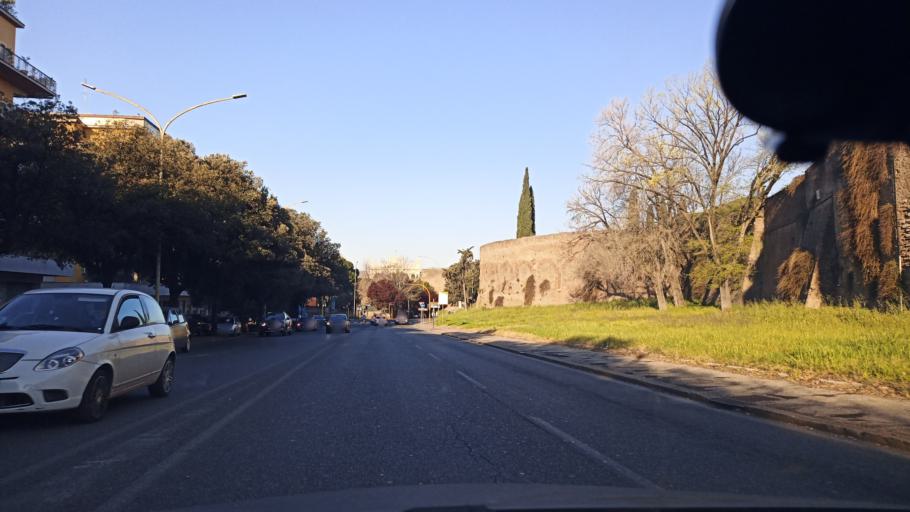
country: IT
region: Latium
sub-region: Citta metropolitana di Roma Capitale
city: Rome
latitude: 41.8874
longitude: 12.5166
